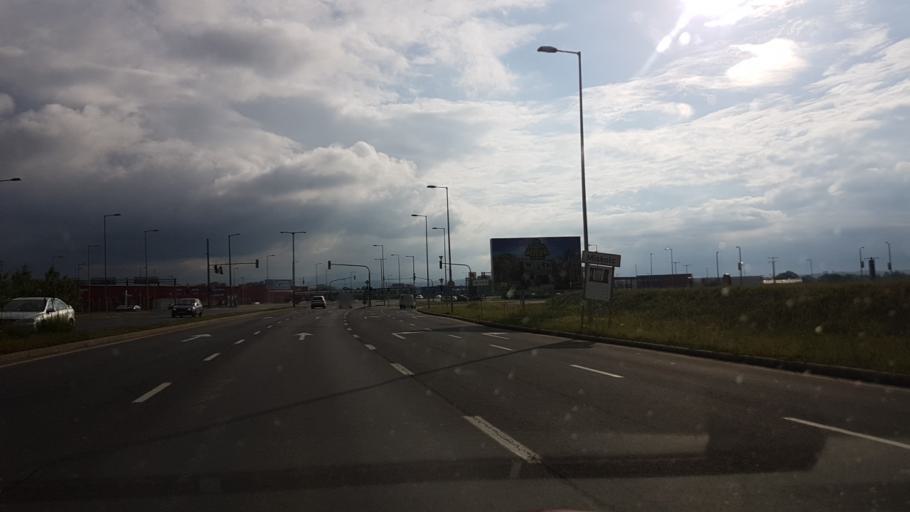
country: HU
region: Borsod-Abauj-Zemplen
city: Felsozsolca
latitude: 48.1062
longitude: 20.8394
